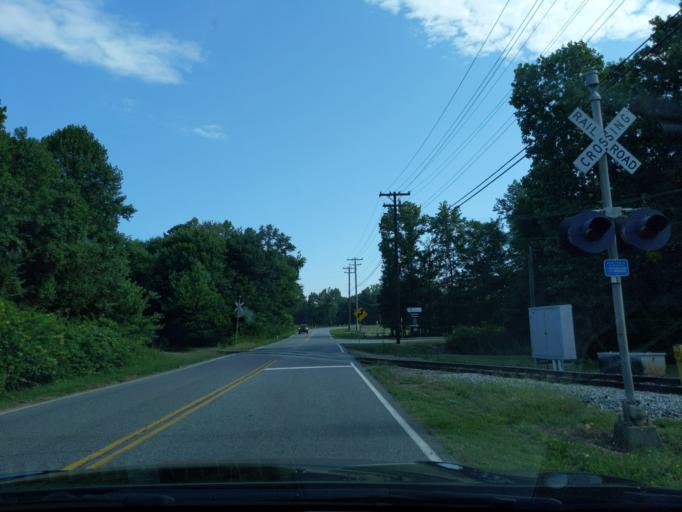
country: US
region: South Carolina
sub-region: Greenville County
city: Mauldin
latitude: 34.8057
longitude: -82.3117
